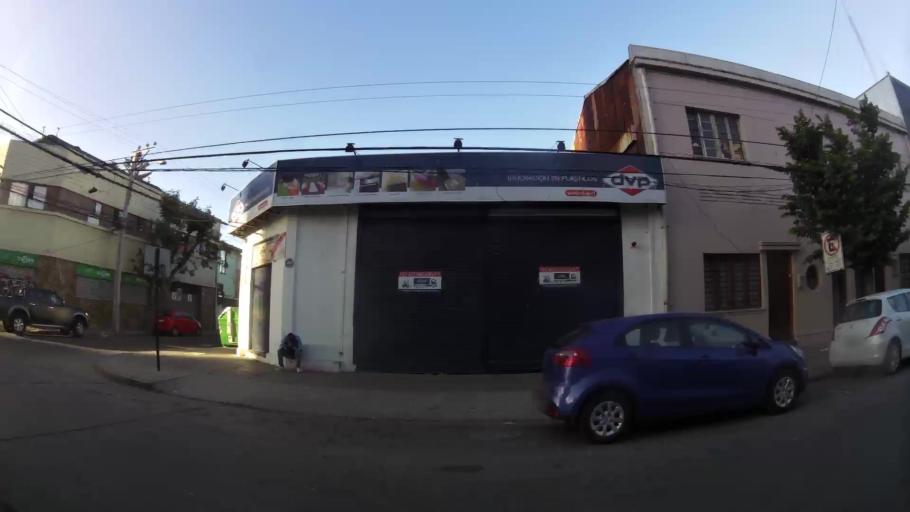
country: CL
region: Valparaiso
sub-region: Provincia de Valparaiso
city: Vina del Mar
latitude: -33.0261
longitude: -71.5447
